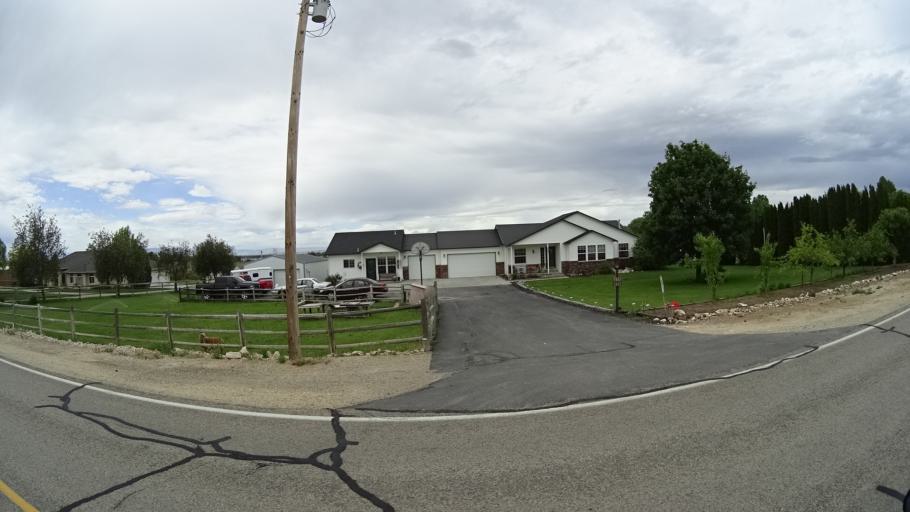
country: US
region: Idaho
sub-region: Ada County
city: Kuna
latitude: 43.5516
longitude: -116.4140
